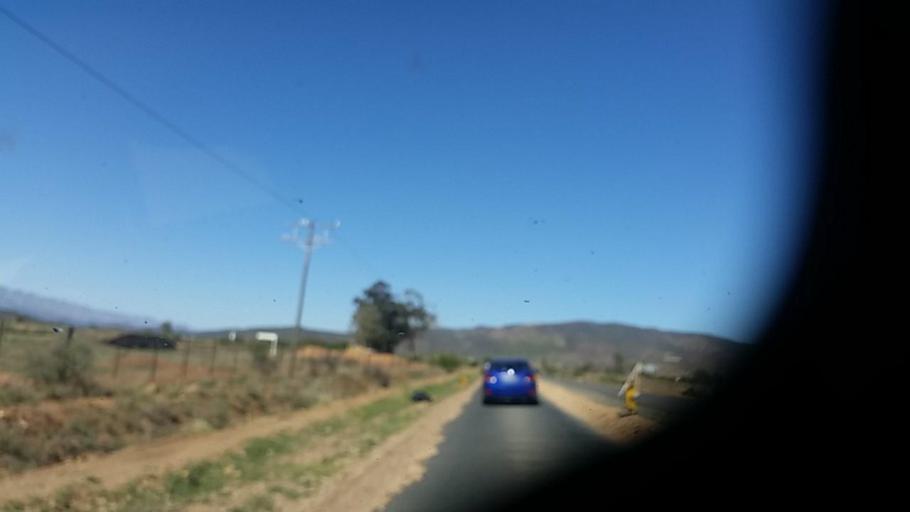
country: ZA
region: Western Cape
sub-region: Eden District Municipality
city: Oudtshoorn
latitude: -33.5616
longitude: 22.4079
